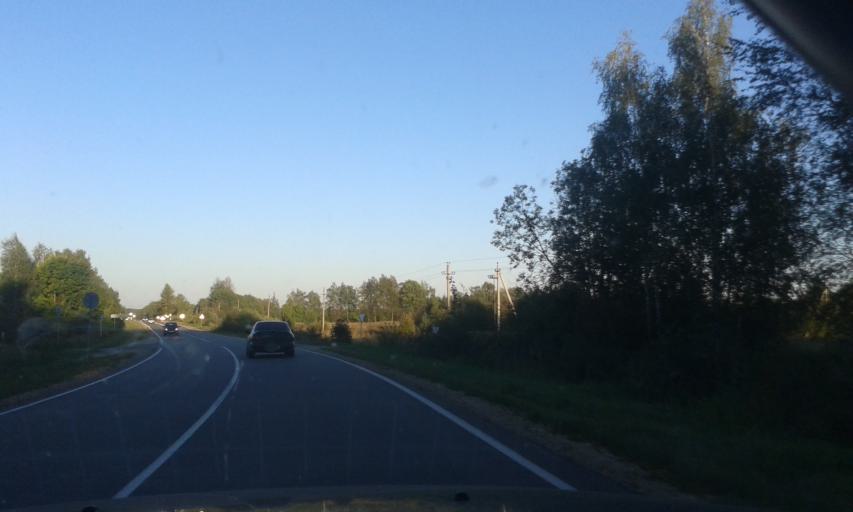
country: RU
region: Tula
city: Leninskiy
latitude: 54.1326
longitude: 37.2942
